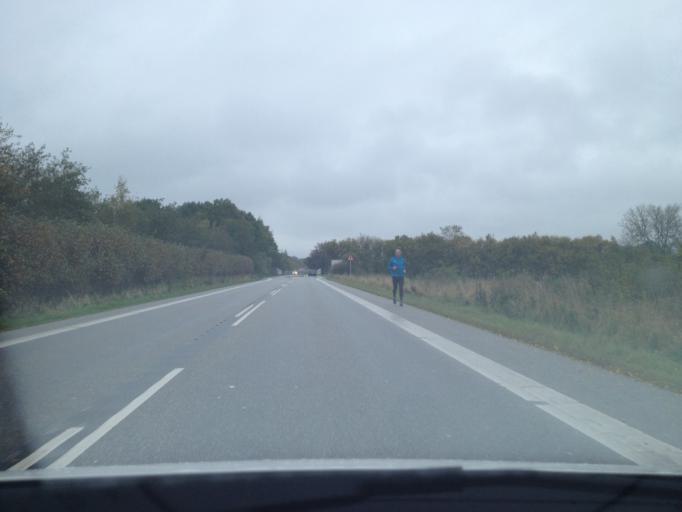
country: DK
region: Capital Region
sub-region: Fredensborg Kommune
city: Fredensborg
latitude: 55.9616
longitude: 12.4097
